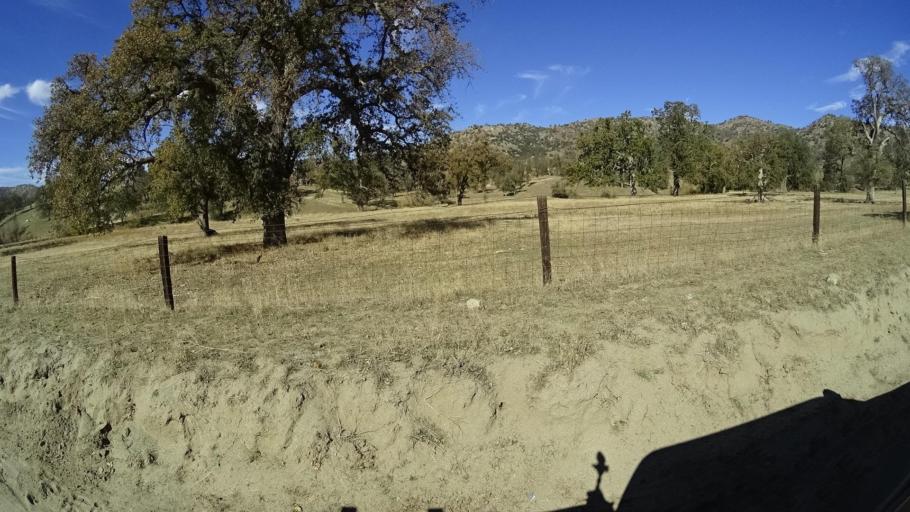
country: US
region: California
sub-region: Kern County
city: Alta Sierra
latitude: 35.6191
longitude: -118.7263
